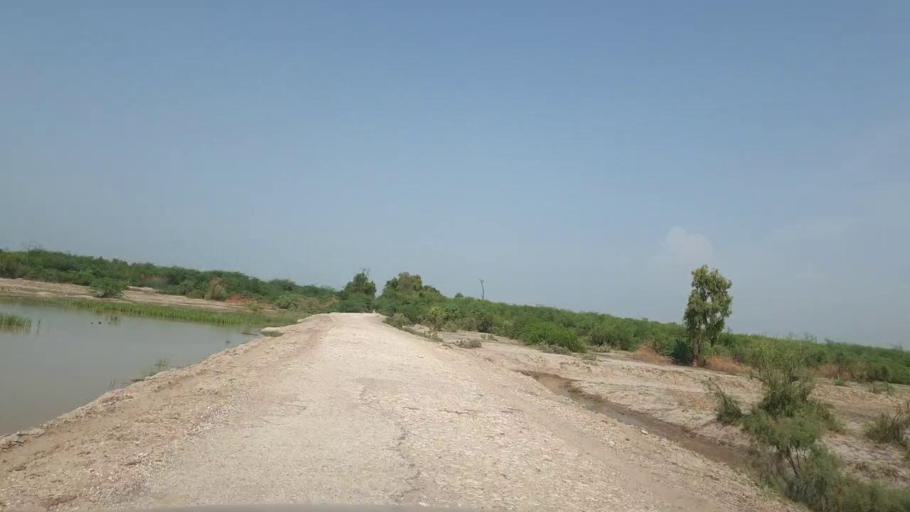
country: PK
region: Sindh
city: Pano Aqil
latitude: 27.7567
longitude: 69.1800
